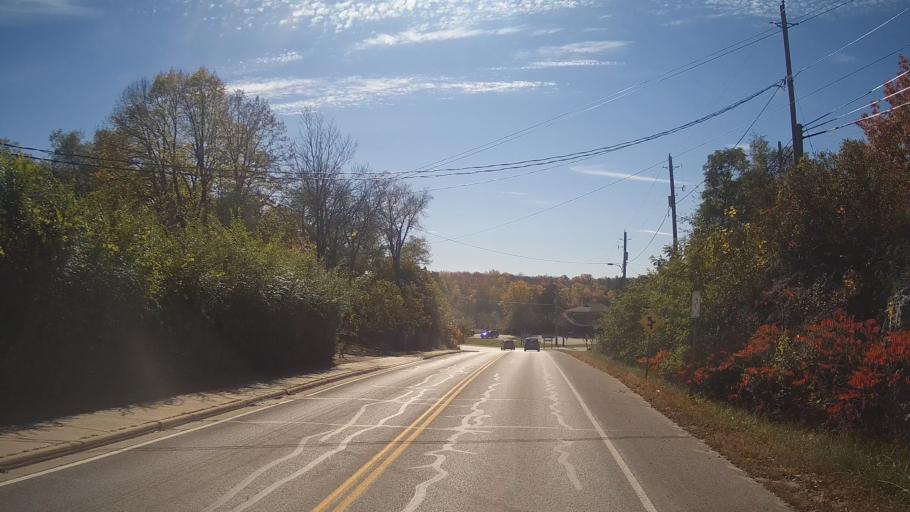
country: CA
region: Ontario
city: Perth
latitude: 44.7694
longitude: -76.6895
